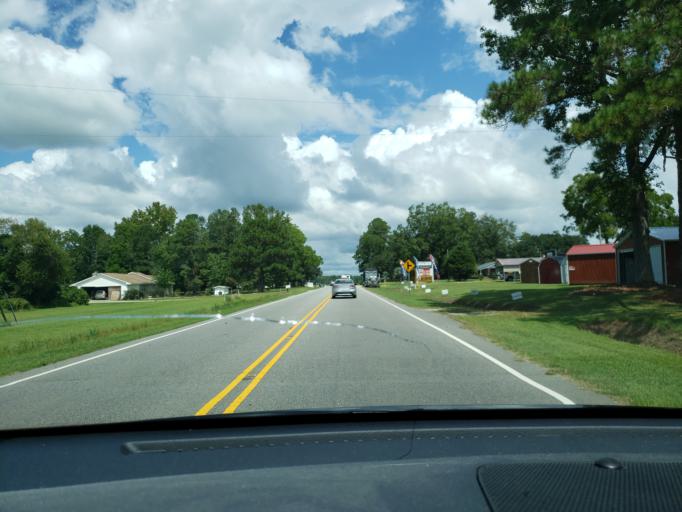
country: US
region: North Carolina
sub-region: Columbus County
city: Brunswick
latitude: 34.2693
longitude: -78.7419
